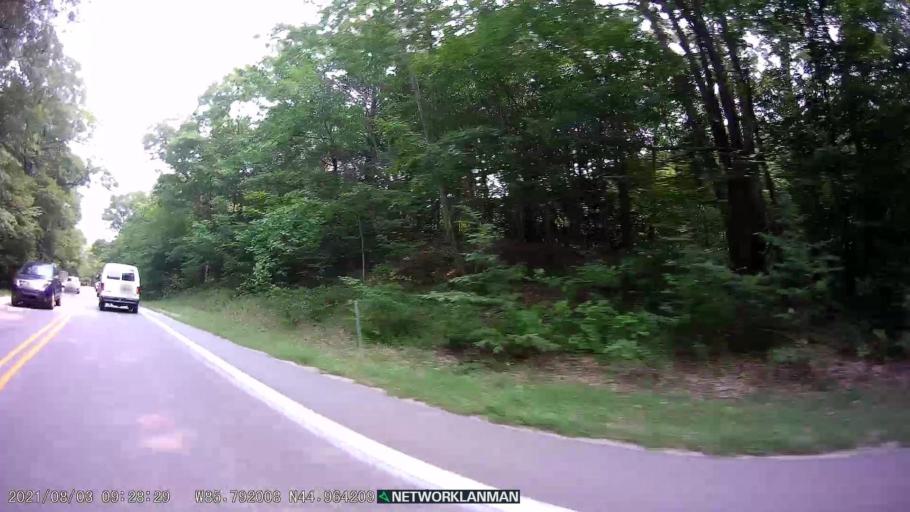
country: US
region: Michigan
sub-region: Leelanau County
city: Leland
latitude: 44.9641
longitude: -85.7915
